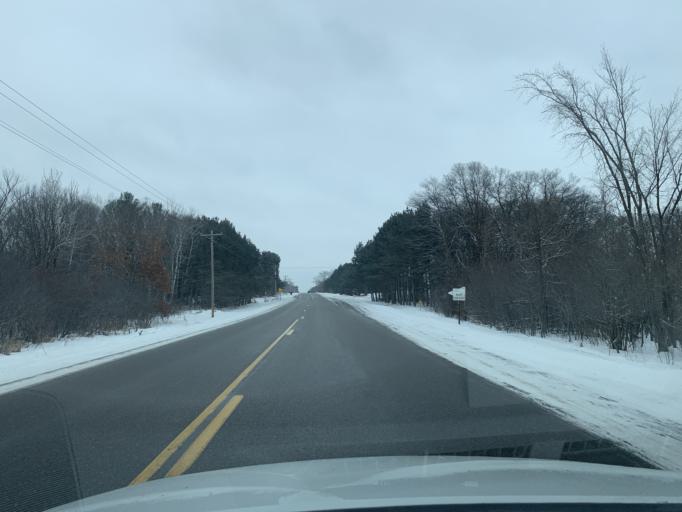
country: US
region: Minnesota
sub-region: Sherburne County
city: Zimmerman
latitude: 45.5013
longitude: -93.6155
